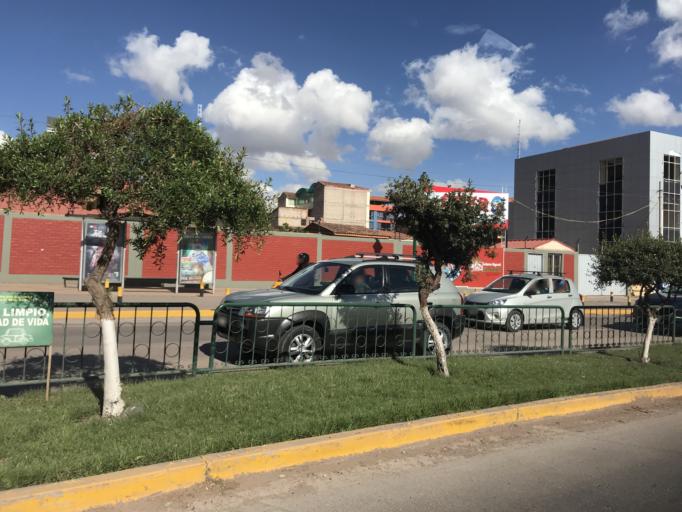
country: PE
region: Cusco
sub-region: Provincia de Cusco
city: Cusco
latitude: -13.5358
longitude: -71.9556
